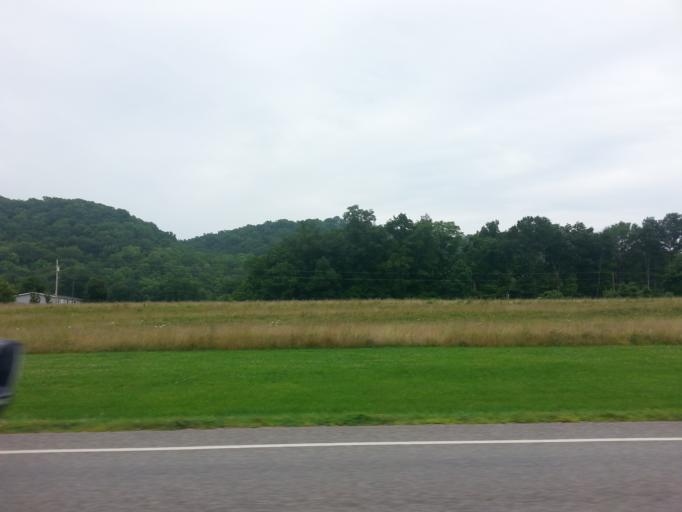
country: US
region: Ohio
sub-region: Brown County
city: Aberdeen
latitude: 38.6926
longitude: -83.7803
